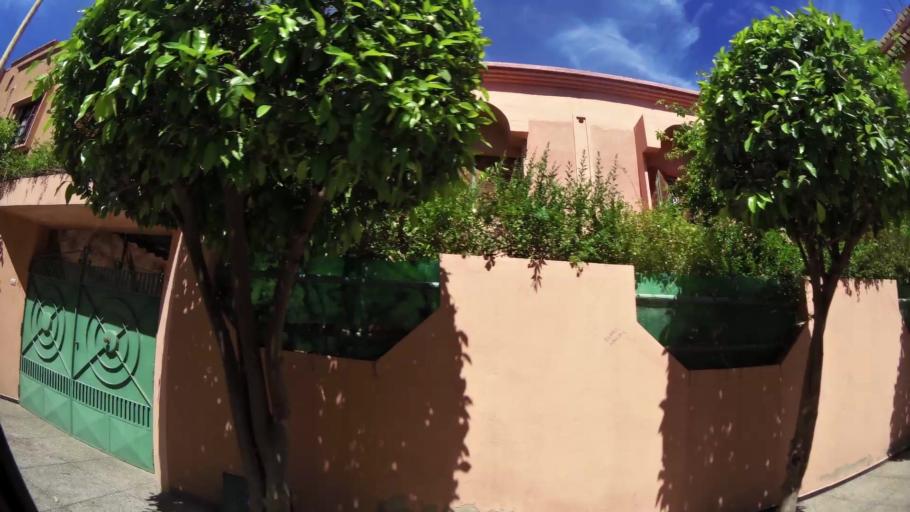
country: MA
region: Marrakech-Tensift-Al Haouz
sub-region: Marrakech
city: Marrakesh
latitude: 31.6636
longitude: -8.0040
